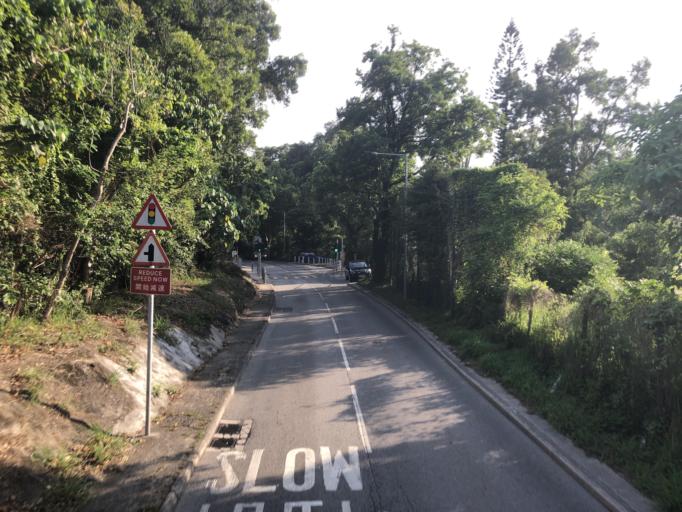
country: HK
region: Tai Po
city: Tai Po
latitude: 22.4910
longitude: 114.1177
